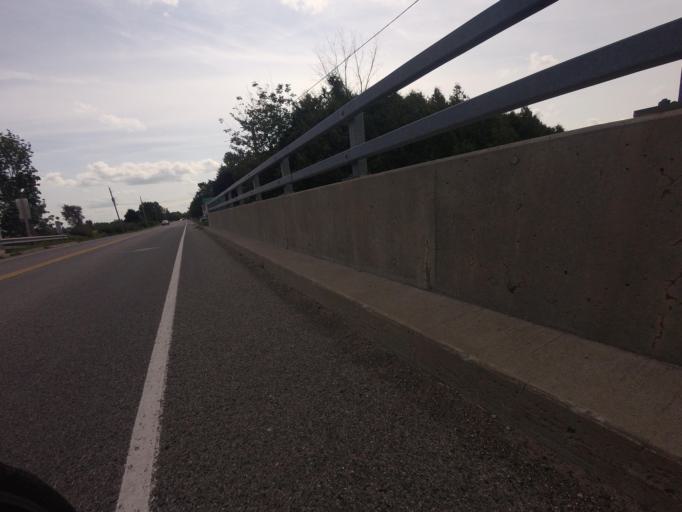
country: CA
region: Ontario
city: Waterloo
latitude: 43.5921
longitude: -80.4635
